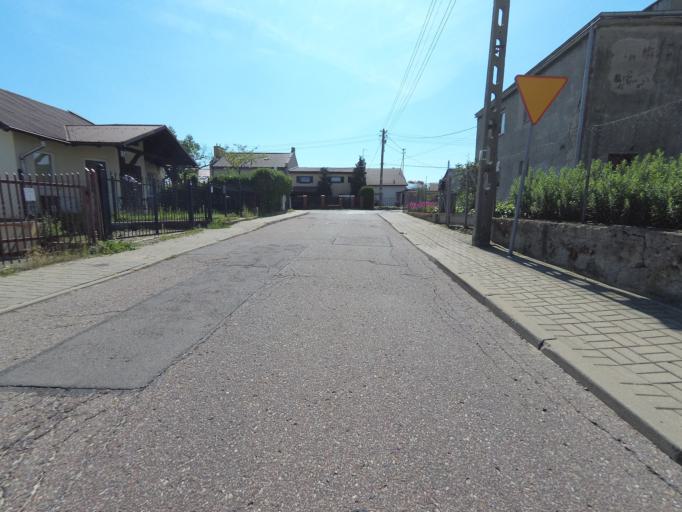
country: PL
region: Pomeranian Voivodeship
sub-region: Gdynia
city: Gdynia
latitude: 54.4936
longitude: 18.5163
